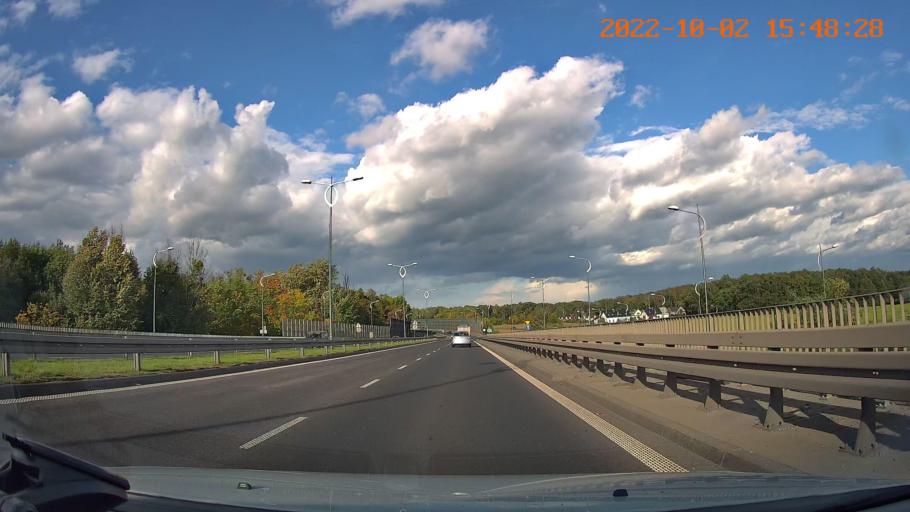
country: PL
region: Silesian Voivodeship
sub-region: Tychy
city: Cielmice
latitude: 50.1095
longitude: 19.0106
